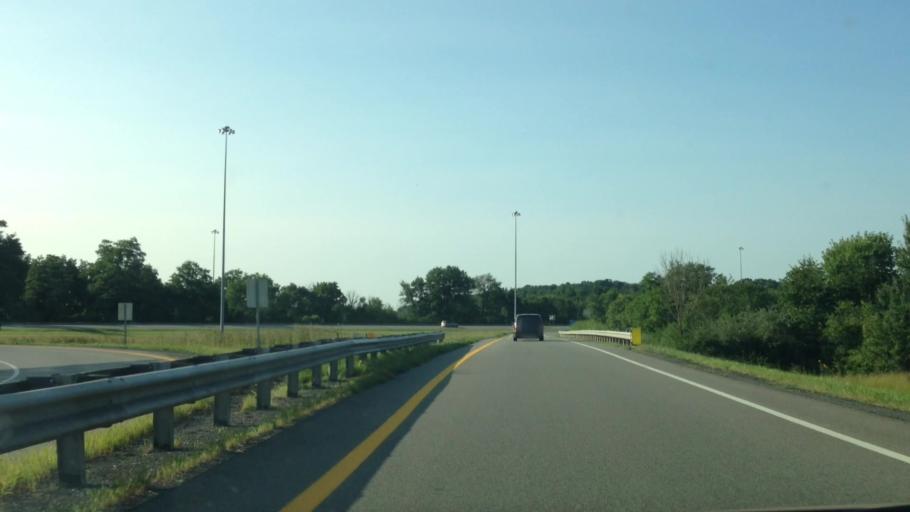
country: US
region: Ohio
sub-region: Summit County
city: Montrose-Ghent
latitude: 41.1375
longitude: -81.6482
